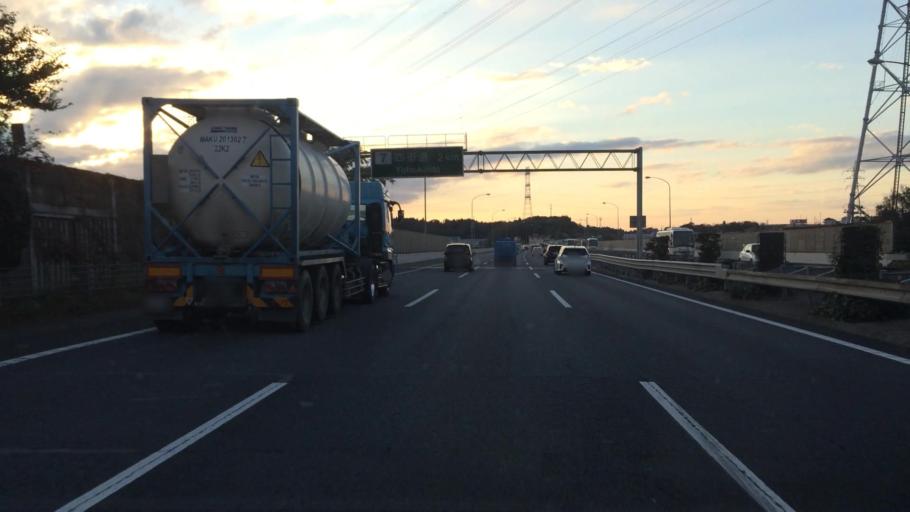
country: JP
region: Chiba
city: Sakura
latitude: 35.6822
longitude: 140.2059
